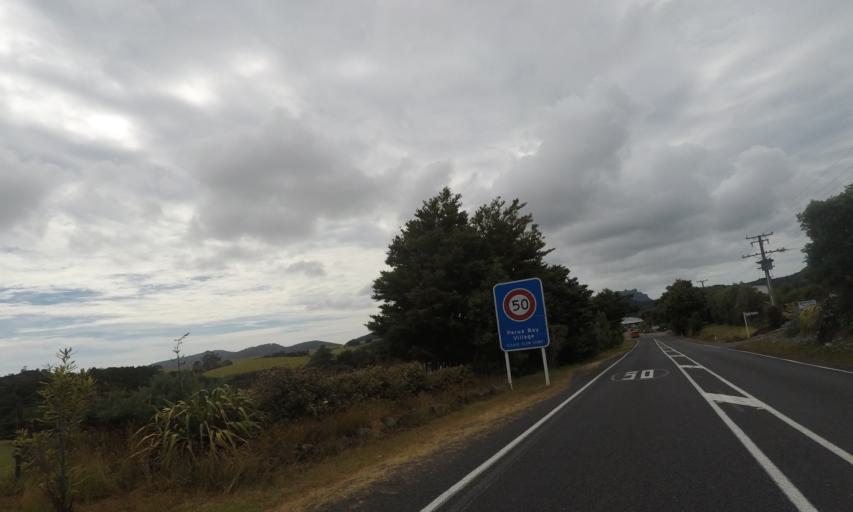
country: NZ
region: Northland
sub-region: Whangarei
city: Ruakaka
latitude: -35.7661
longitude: 174.4750
